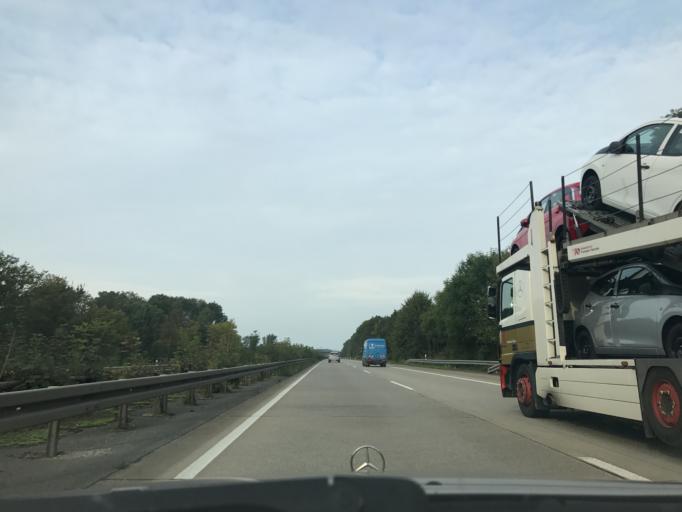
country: DE
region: North Rhine-Westphalia
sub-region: Regierungsbezirk Arnsberg
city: Anrochte
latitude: 51.5853
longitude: 8.3531
